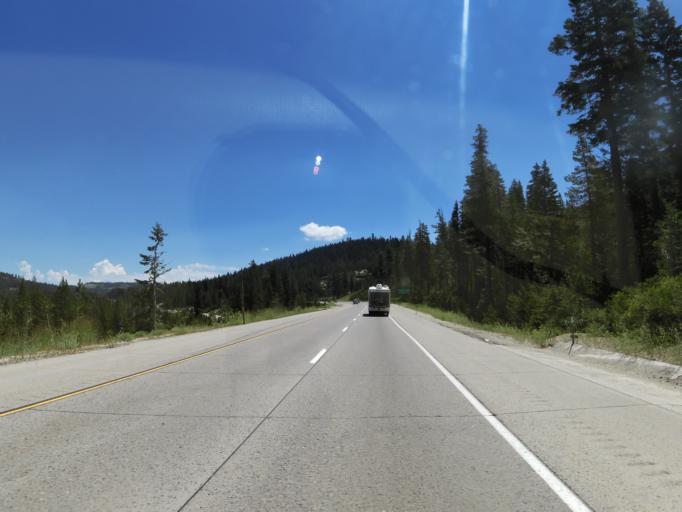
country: US
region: California
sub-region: Nevada County
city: Truckee
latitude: 39.3231
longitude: -120.4107
